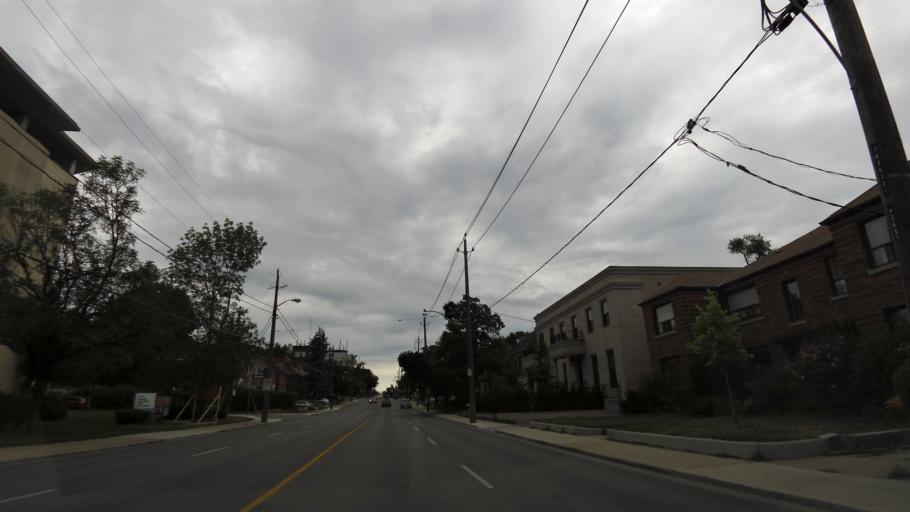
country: CA
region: Ontario
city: Toronto
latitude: 43.6956
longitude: -79.4234
